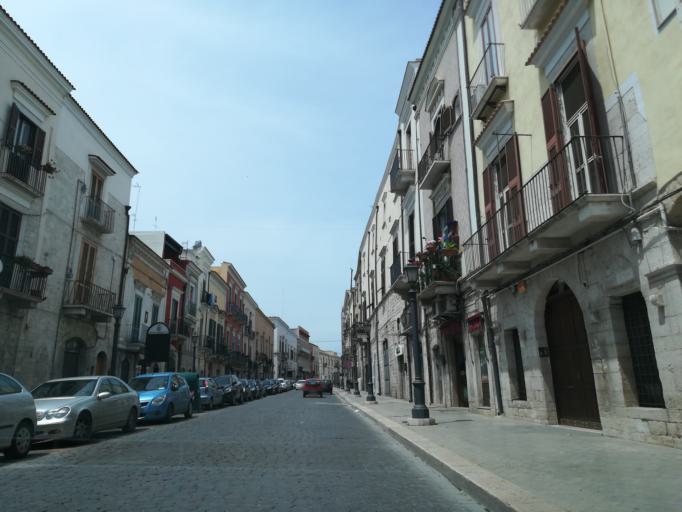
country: IT
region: Apulia
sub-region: Provincia di Barletta - Andria - Trani
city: Barletta
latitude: 41.3193
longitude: 16.2861
